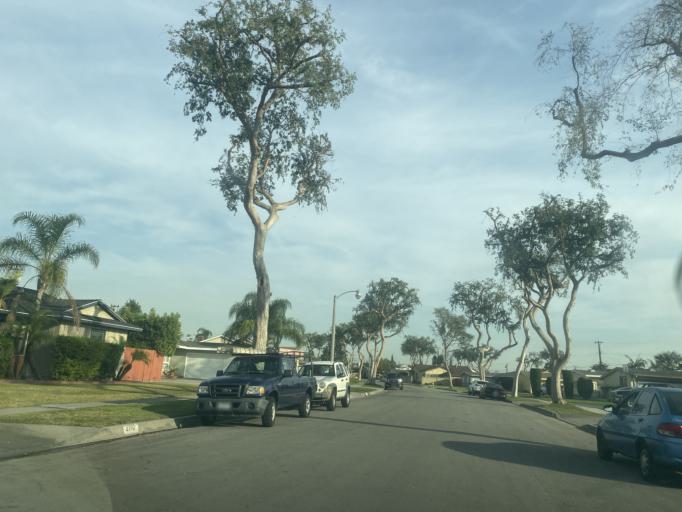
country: US
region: California
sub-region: Orange County
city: Buena Park
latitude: 33.8556
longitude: -117.9659
